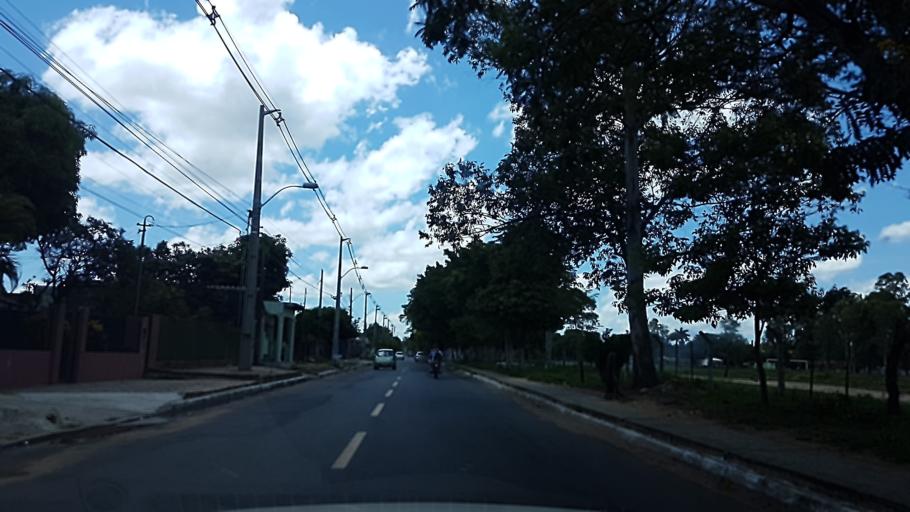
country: PY
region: Central
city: Colonia Mariano Roque Alonso
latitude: -25.2459
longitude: -57.5467
